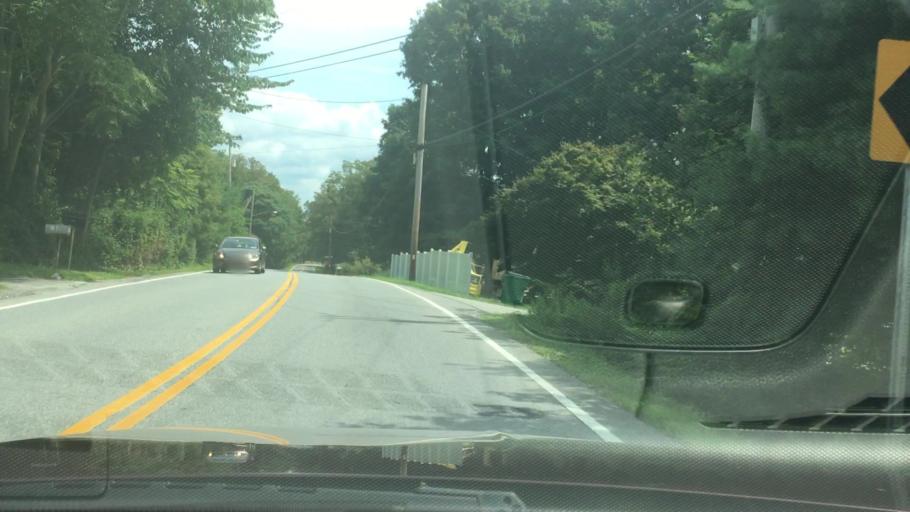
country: US
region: New York
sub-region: Dutchess County
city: Hillside Lake
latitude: 41.6481
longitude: -73.8243
